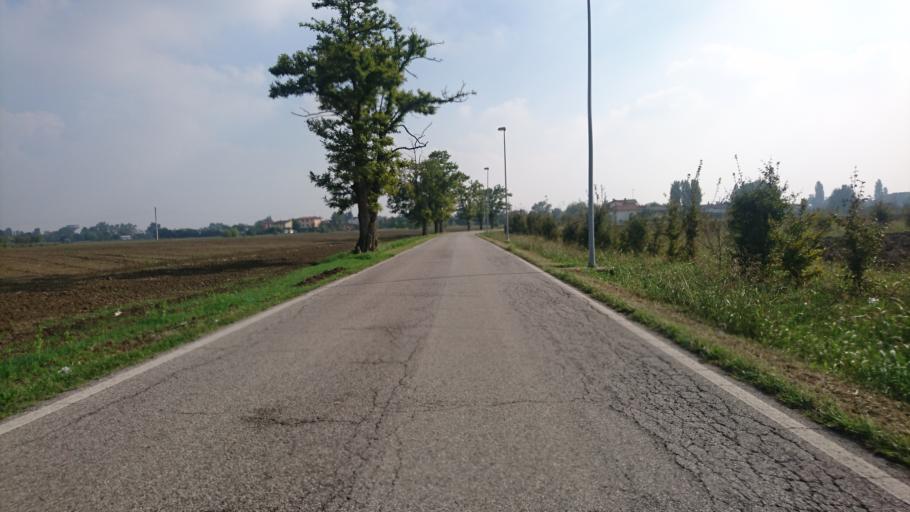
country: IT
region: Veneto
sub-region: Provincia di Rovigo
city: Rovigo
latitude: 45.0509
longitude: 11.7760
